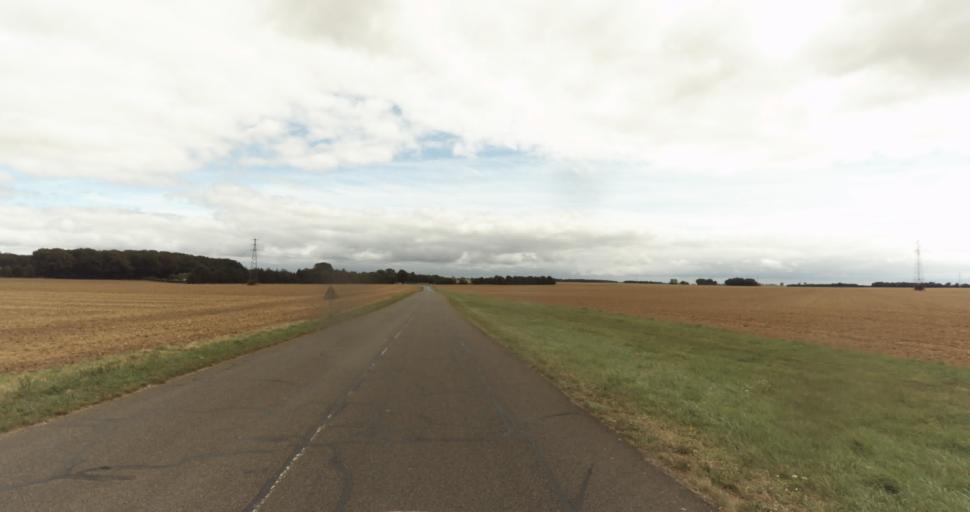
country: FR
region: Haute-Normandie
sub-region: Departement de l'Eure
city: Evreux
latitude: 48.9178
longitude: 1.1982
